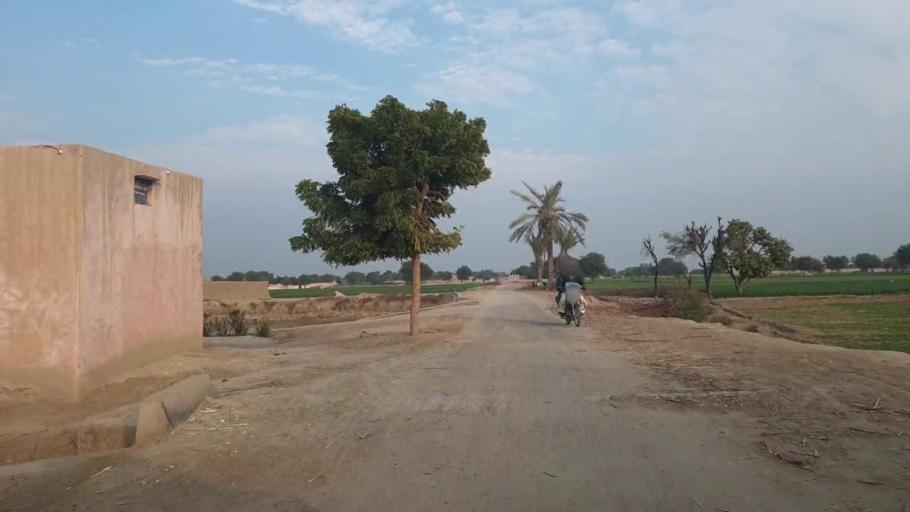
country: PK
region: Sindh
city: Shahpur Chakar
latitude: 26.1095
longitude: 68.5473
